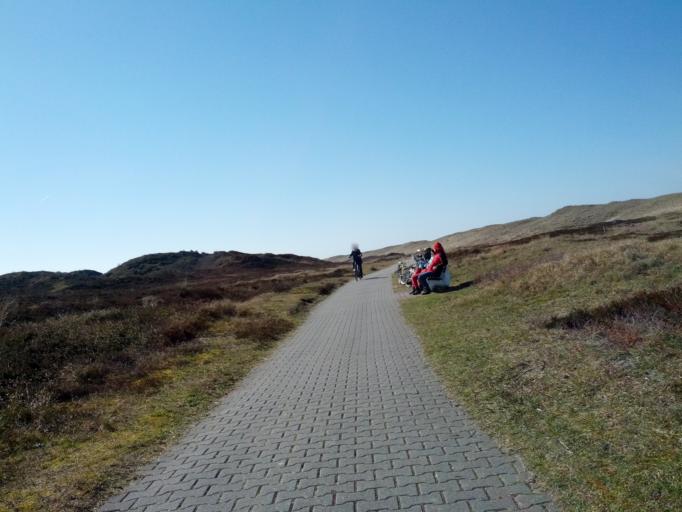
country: DE
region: Lower Saxony
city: Langeoog
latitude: 53.7540
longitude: 7.5054
